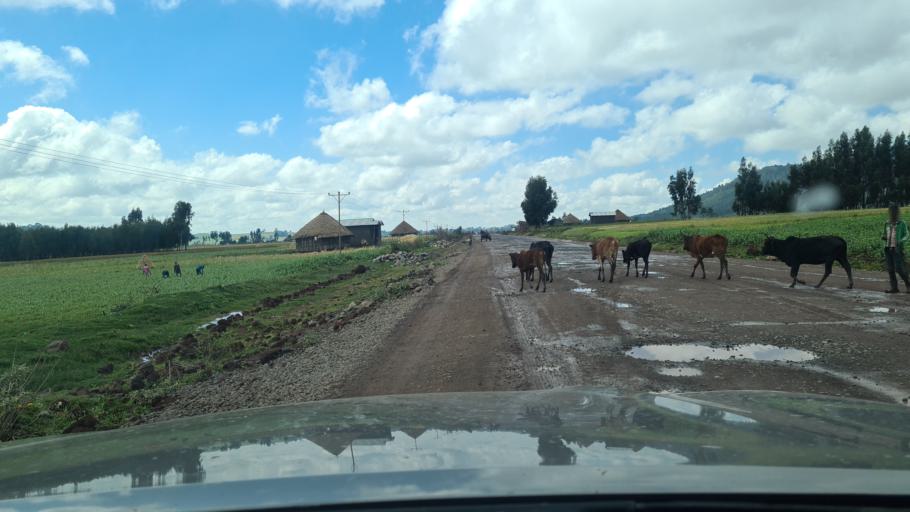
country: ET
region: Oromiya
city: Huruta
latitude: 8.0876
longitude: 39.5400
